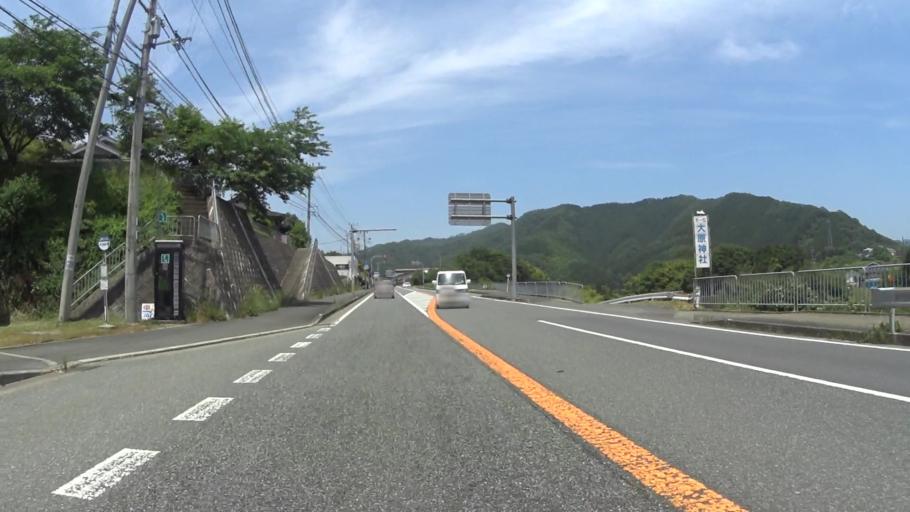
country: JP
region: Kyoto
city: Ayabe
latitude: 35.2238
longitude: 135.2251
